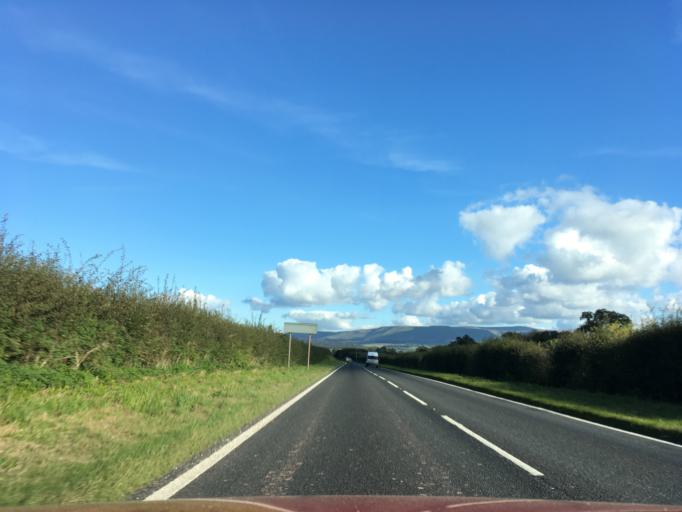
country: GB
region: Wales
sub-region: Sir Powys
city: Brecon
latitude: 51.9971
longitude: -3.2977
